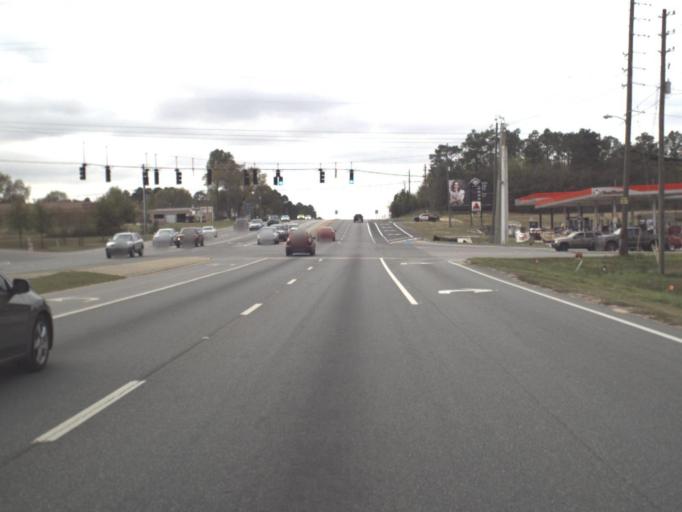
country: US
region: Florida
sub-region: Okaloosa County
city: Crestview
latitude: 30.7121
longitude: -86.5702
